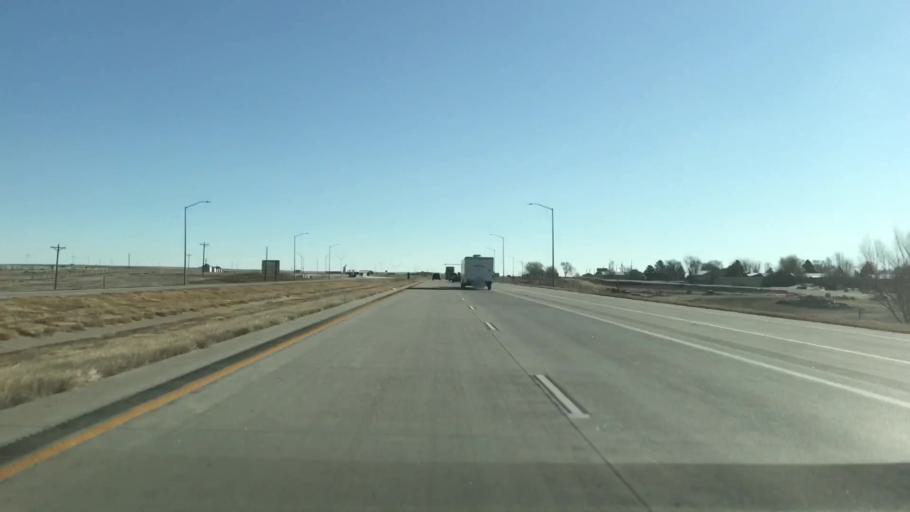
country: US
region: Colorado
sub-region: Lincoln County
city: Limon
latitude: 39.2734
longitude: -103.6917
